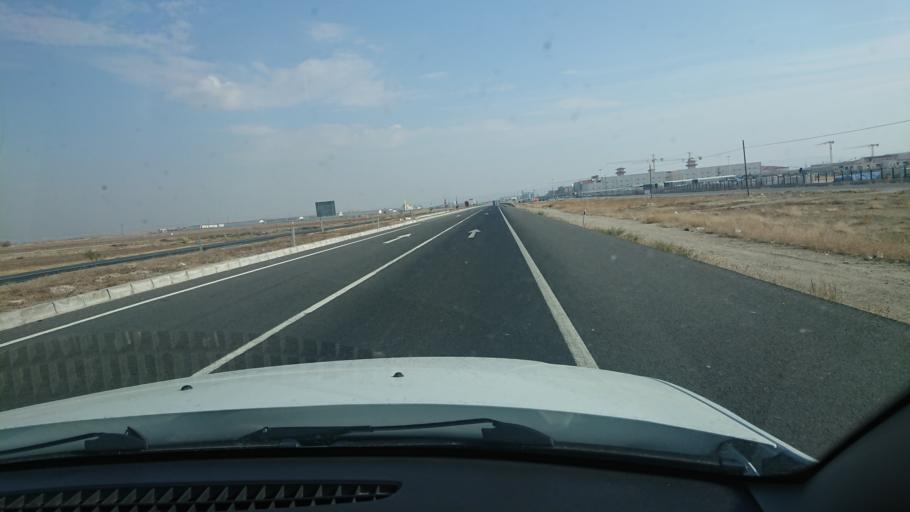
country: TR
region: Aksaray
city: Aksaray
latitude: 38.3334
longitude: 33.9208
